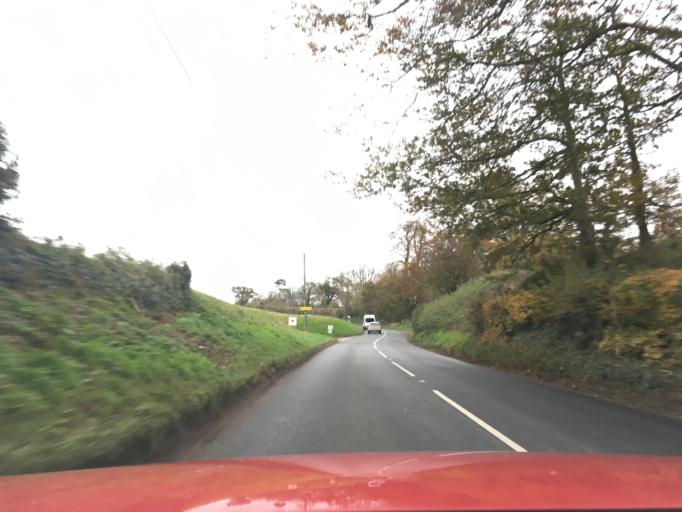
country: GB
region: England
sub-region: Dorset
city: Sherborne
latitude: 50.9647
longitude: -2.5486
